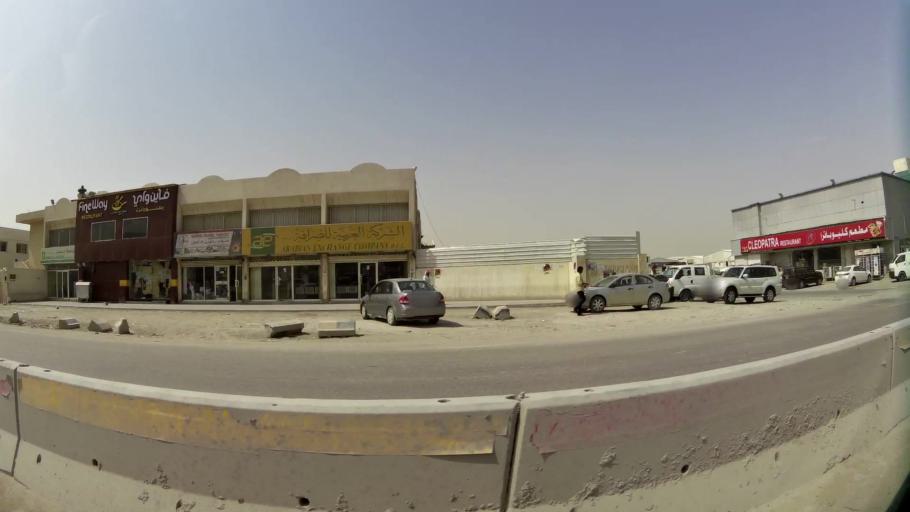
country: QA
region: Baladiyat ar Rayyan
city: Ar Rayyan
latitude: 25.1980
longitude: 51.4298
